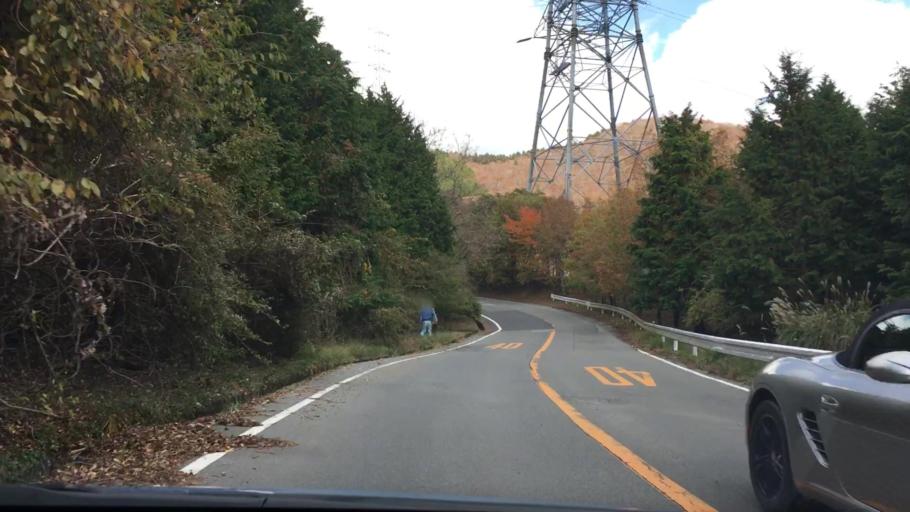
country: JP
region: Shizuoka
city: Gotemba
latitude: 35.3936
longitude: 138.9429
